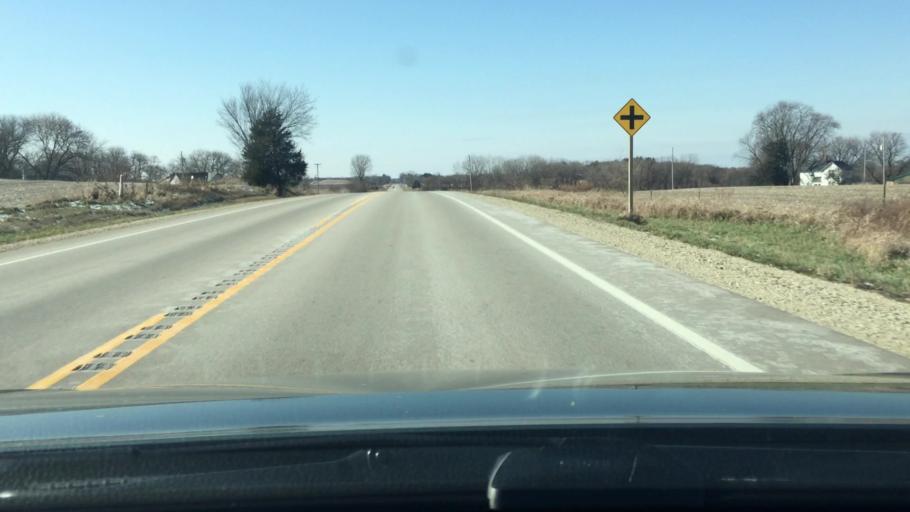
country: US
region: Wisconsin
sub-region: Jefferson County
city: Lake Mills
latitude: 43.0077
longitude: -88.9013
